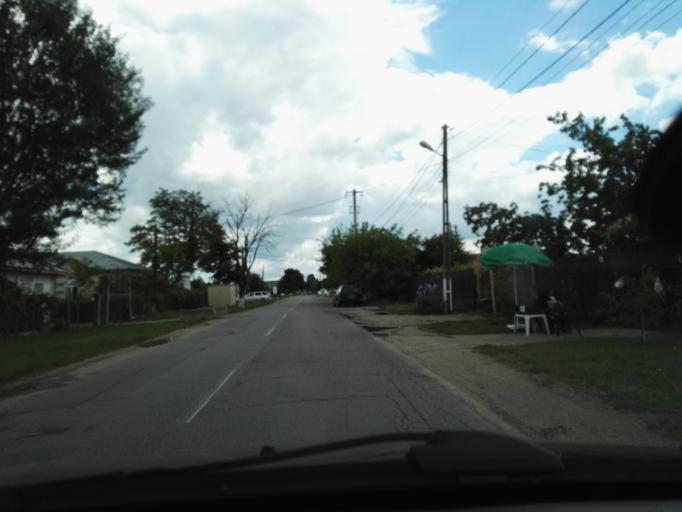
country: RO
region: Ilfov
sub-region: Comuna Copaceni
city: Copaceni
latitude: 44.2427
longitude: 26.1020
